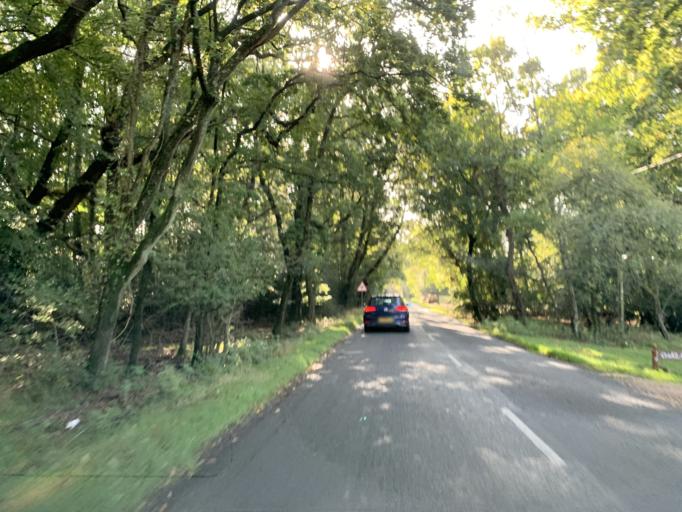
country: GB
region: England
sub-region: Wiltshire
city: Downton
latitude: 50.9683
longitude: -1.7069
